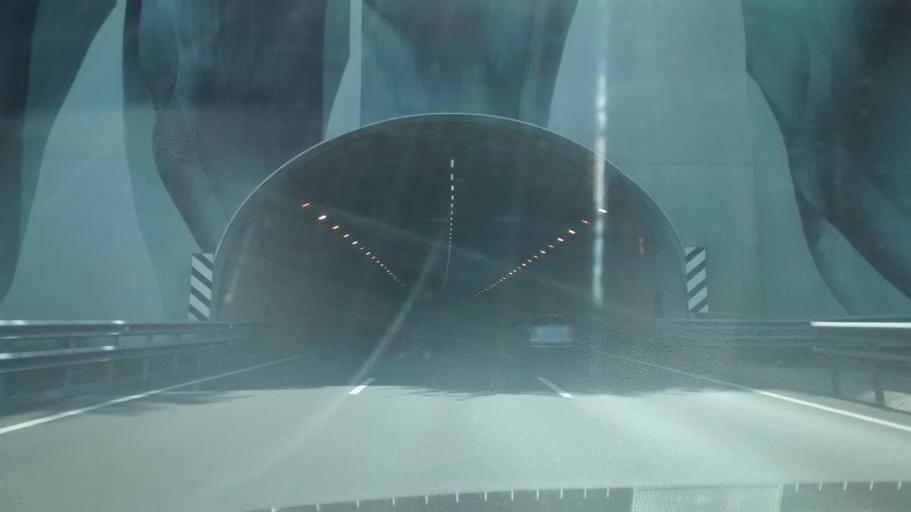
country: ES
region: Basque Country
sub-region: Bizkaia
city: Alonsotegi
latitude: 43.2504
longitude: -2.9735
